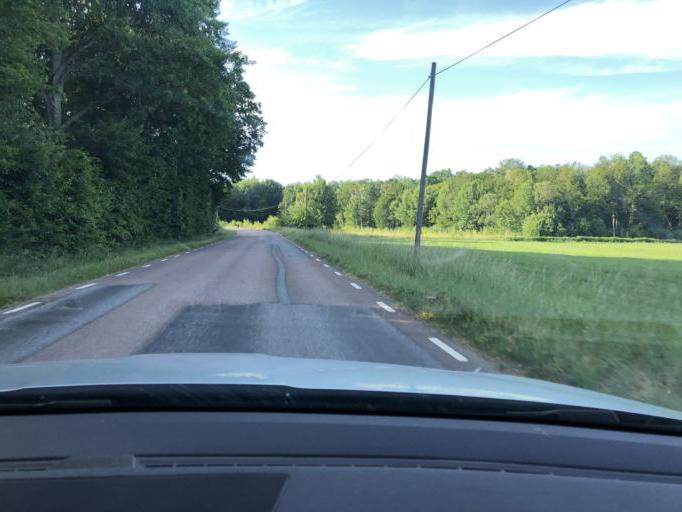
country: SE
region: Blekinge
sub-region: Solvesborgs Kommun
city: Soelvesborg
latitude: 56.1402
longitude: 14.6068
